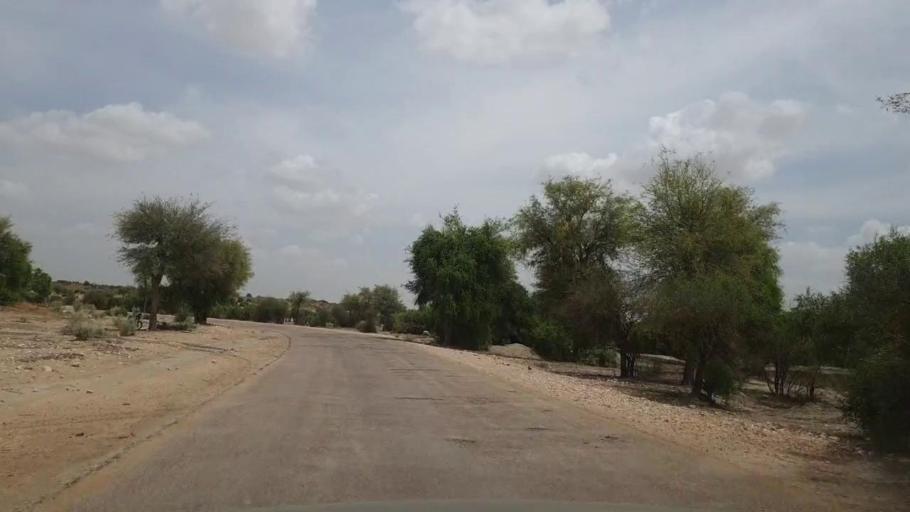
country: PK
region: Sindh
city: Kot Diji
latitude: 27.1804
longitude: 69.1742
